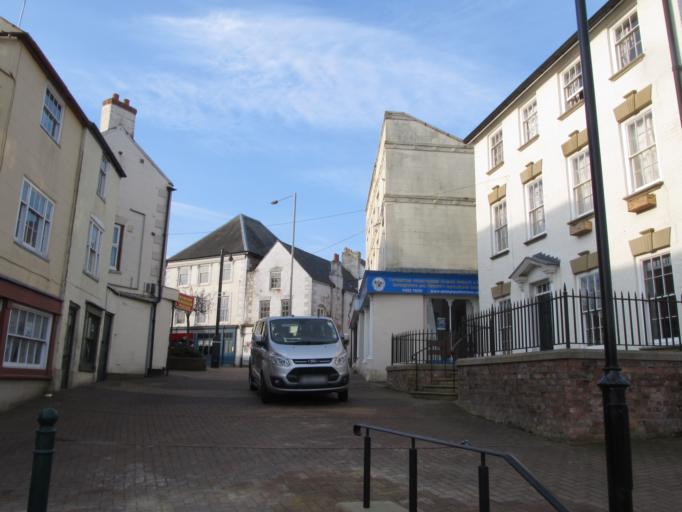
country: GB
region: Wales
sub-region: County of Flintshire
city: Holywell
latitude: 53.2746
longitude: -3.2231
